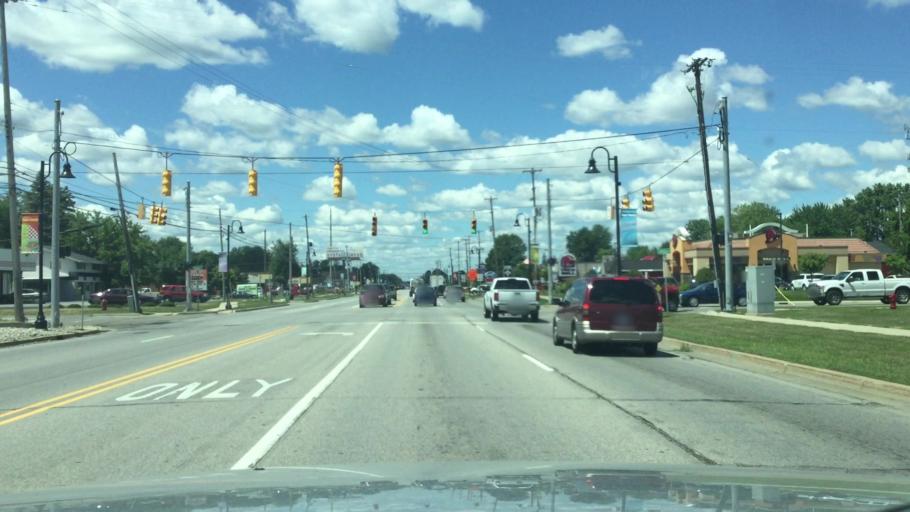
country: US
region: Michigan
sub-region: Saginaw County
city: Shields
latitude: 43.4160
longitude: -84.0709
